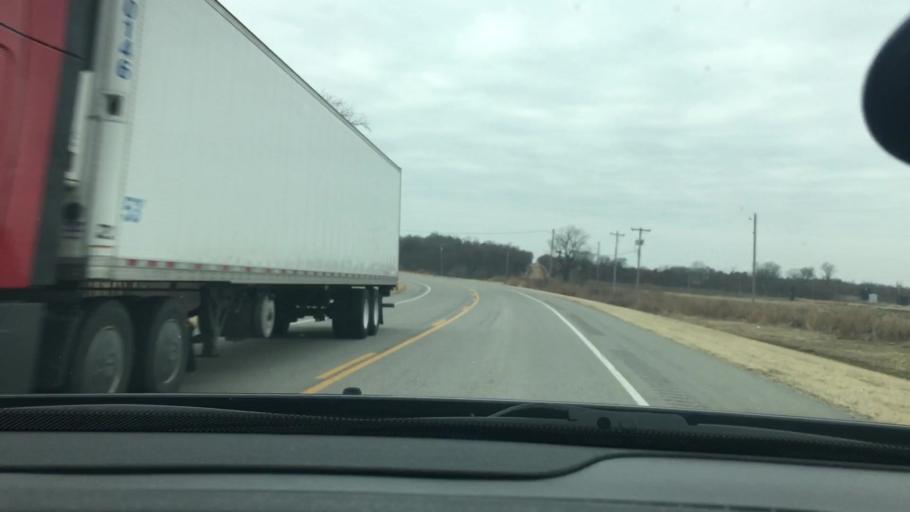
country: US
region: Oklahoma
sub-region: Carter County
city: Healdton
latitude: 34.4925
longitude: -97.4421
